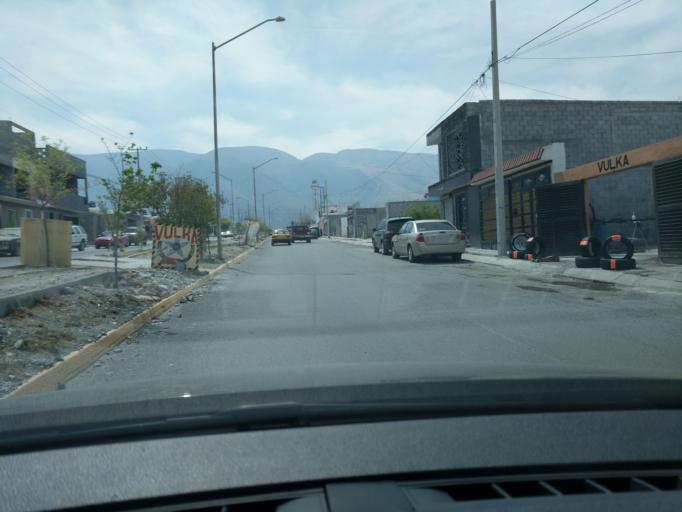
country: MX
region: Coahuila
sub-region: Arteaga
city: Arteaga
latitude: 25.4219
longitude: -100.9015
